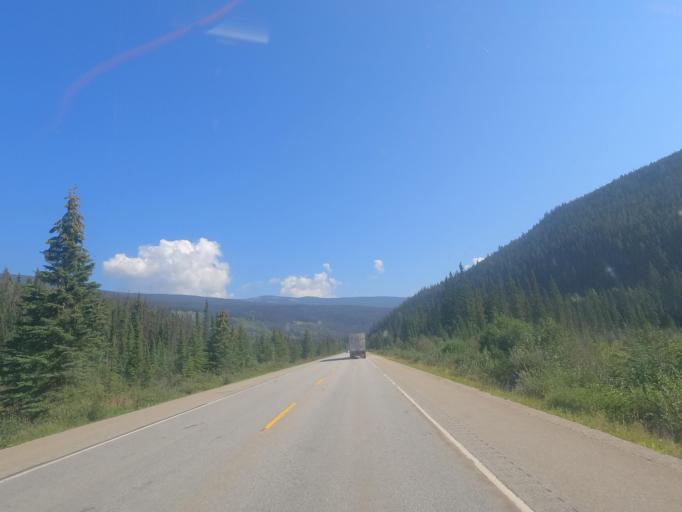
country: CA
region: Alberta
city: Jasper Park Lodge
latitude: 52.8813
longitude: -118.4898
